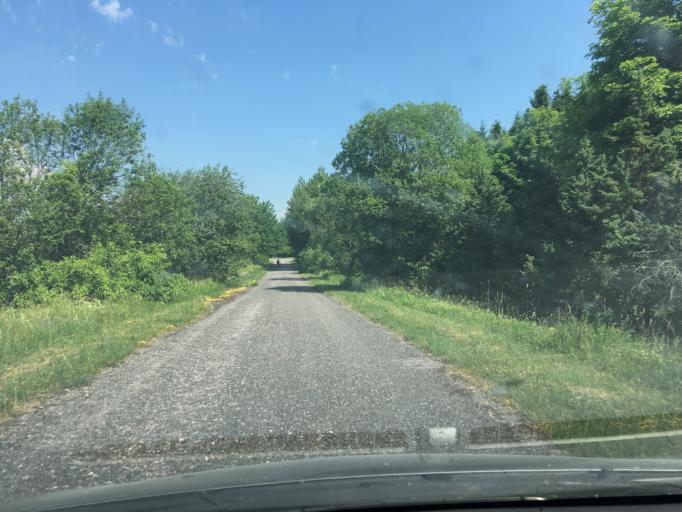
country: EE
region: Laeaene
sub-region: Lihula vald
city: Lihula
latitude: 58.6673
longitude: 23.7642
